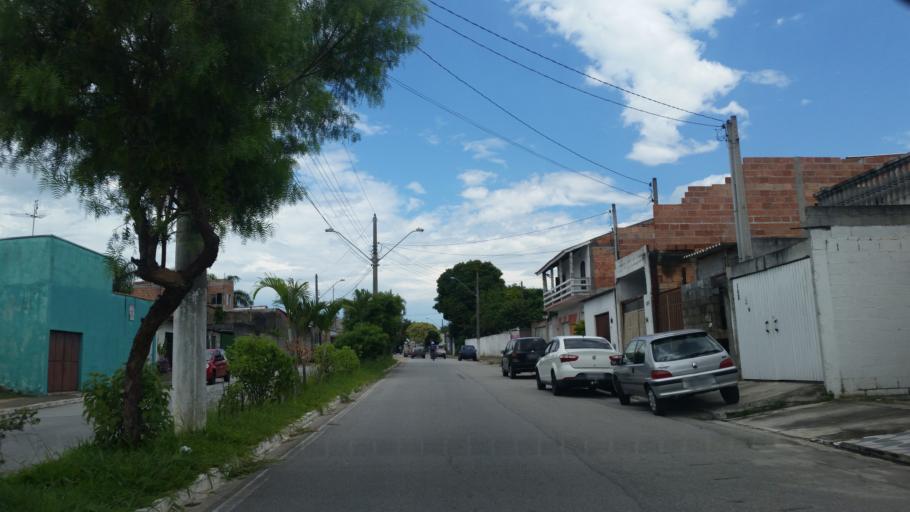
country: BR
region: Sao Paulo
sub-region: Taubate
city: Taubate
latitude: -23.0219
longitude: -45.5726
